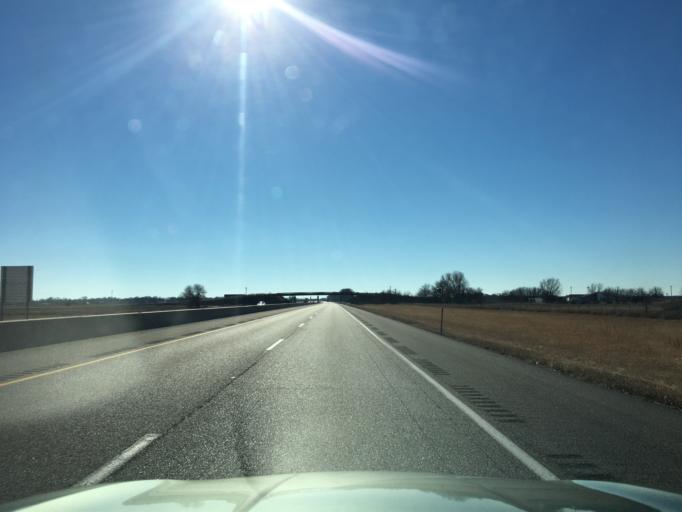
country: US
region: Kansas
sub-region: Sumner County
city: Belle Plaine
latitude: 37.4536
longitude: -97.3223
